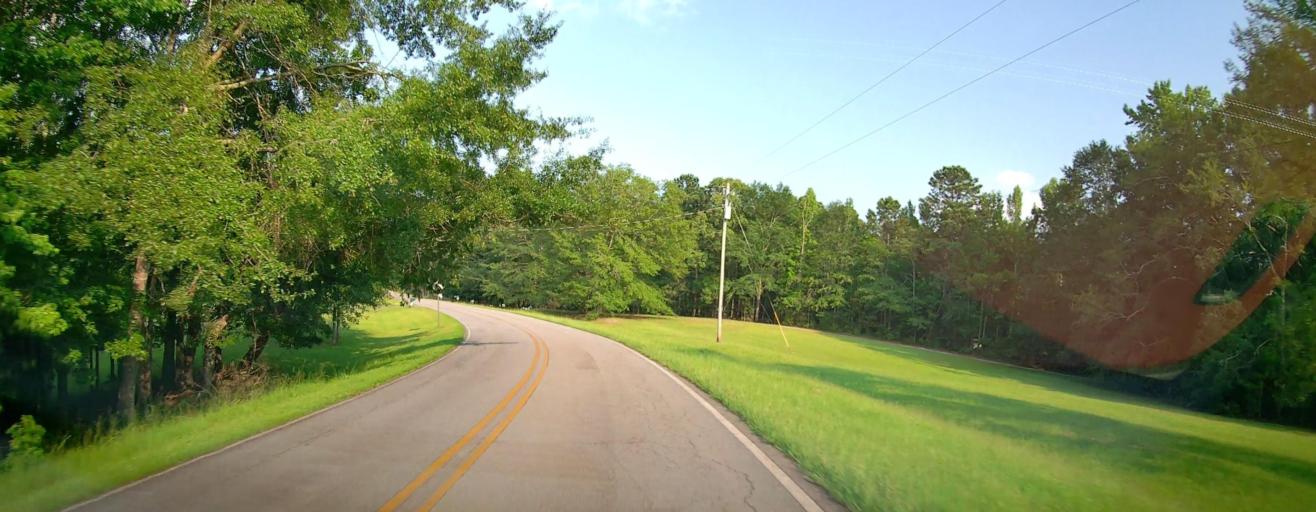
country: US
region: Georgia
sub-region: Monroe County
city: Forsyth
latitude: 32.9960
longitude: -83.7658
